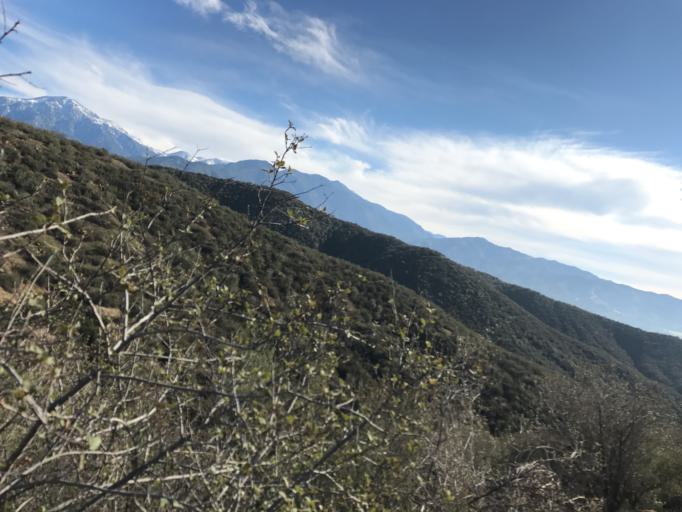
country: US
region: California
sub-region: San Bernardino County
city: Yucaipa
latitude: 34.0596
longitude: -117.0648
